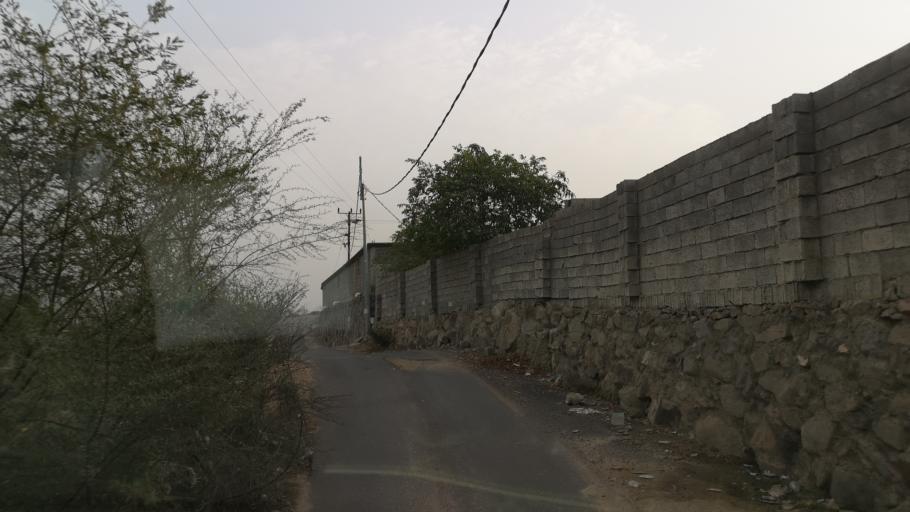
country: YE
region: Sa'dah
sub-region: Monabbih
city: Suq al Khamis
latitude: 17.3748
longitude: 43.1269
